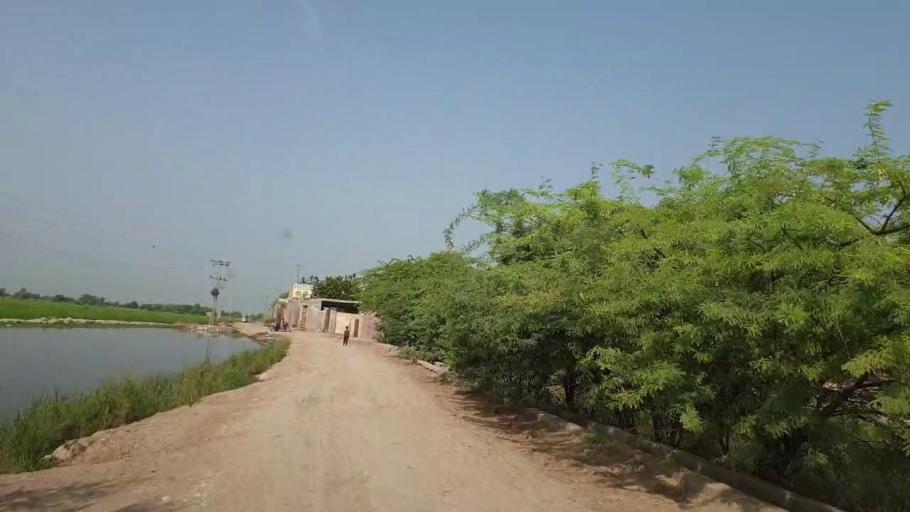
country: PK
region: Sindh
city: Bagarji
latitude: 27.8073
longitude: 68.7474
